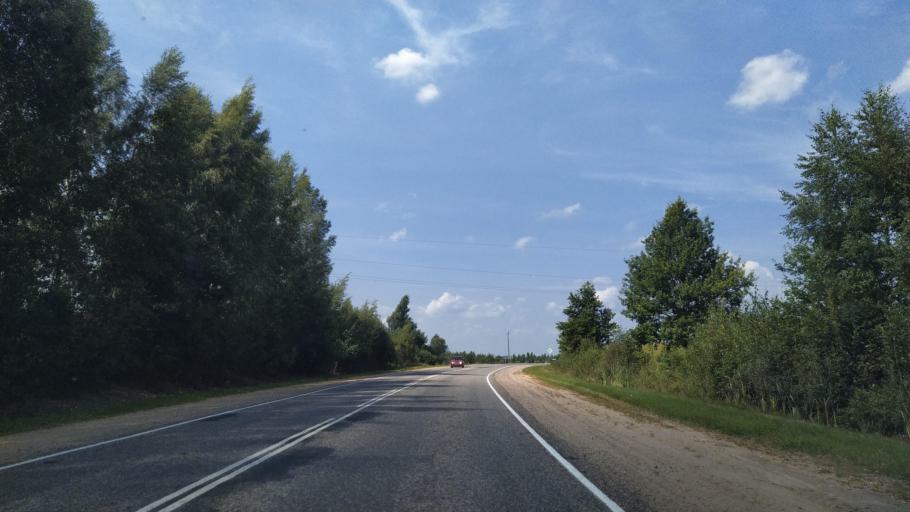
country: RU
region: Pskov
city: Pushkinskiye Gory
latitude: 57.0109
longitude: 28.9069
